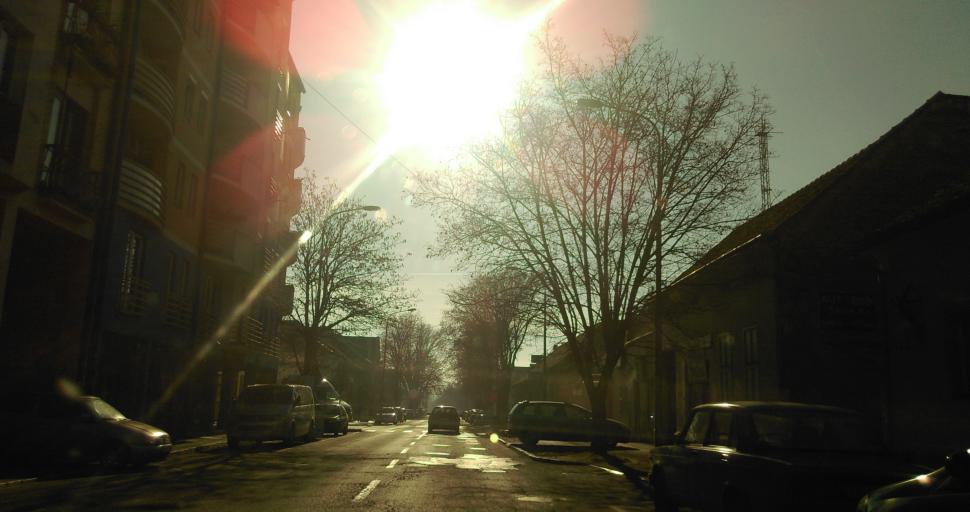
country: RS
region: Autonomna Pokrajina Vojvodina
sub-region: Sremski Okrug
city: Ruma
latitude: 45.0062
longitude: 19.8225
